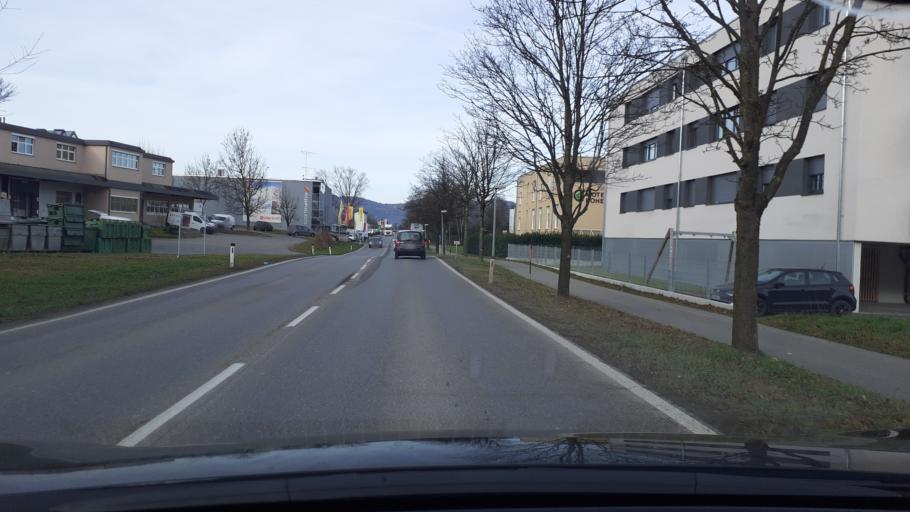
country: AT
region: Vorarlberg
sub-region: Politischer Bezirk Dornbirn
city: Hohenems
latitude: 47.3717
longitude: 9.6821
